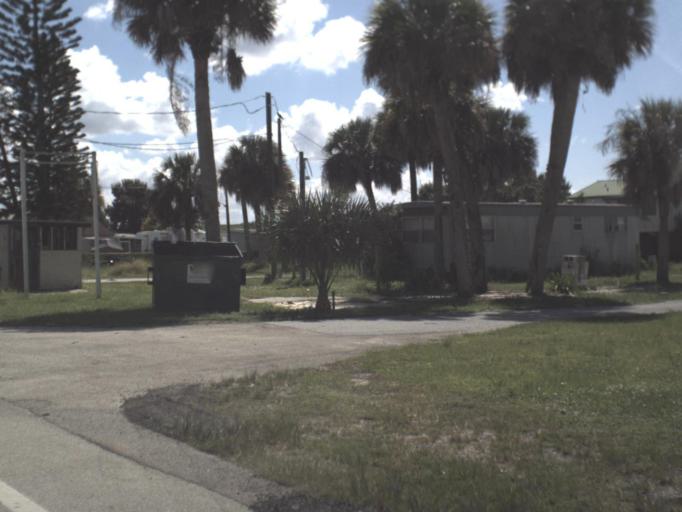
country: US
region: Florida
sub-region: Okeechobee County
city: Taylor Creek
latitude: 27.2014
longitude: -80.7750
